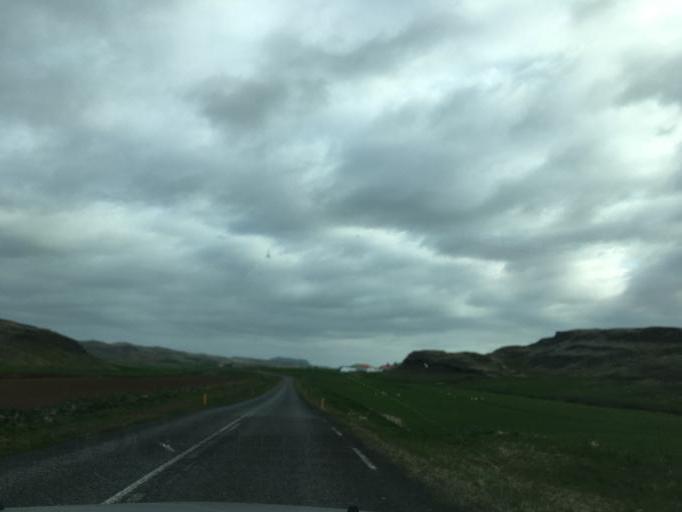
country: IS
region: South
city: Vestmannaeyjar
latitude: 64.2030
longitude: -20.2750
